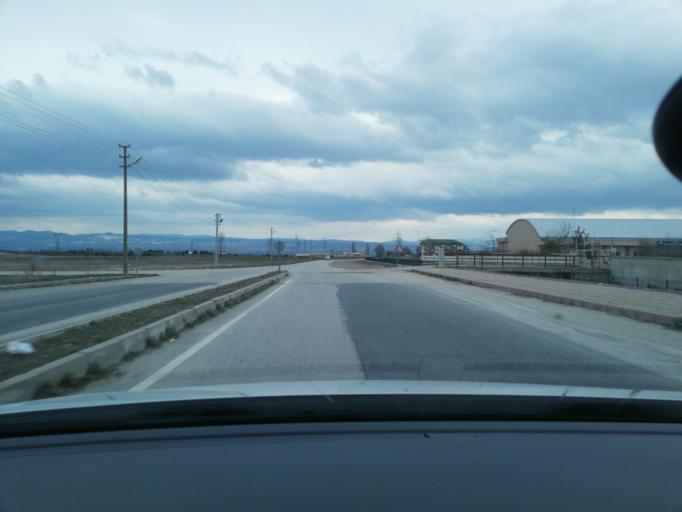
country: TR
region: Bolu
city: Gerede
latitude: 40.7860
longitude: 32.2042
